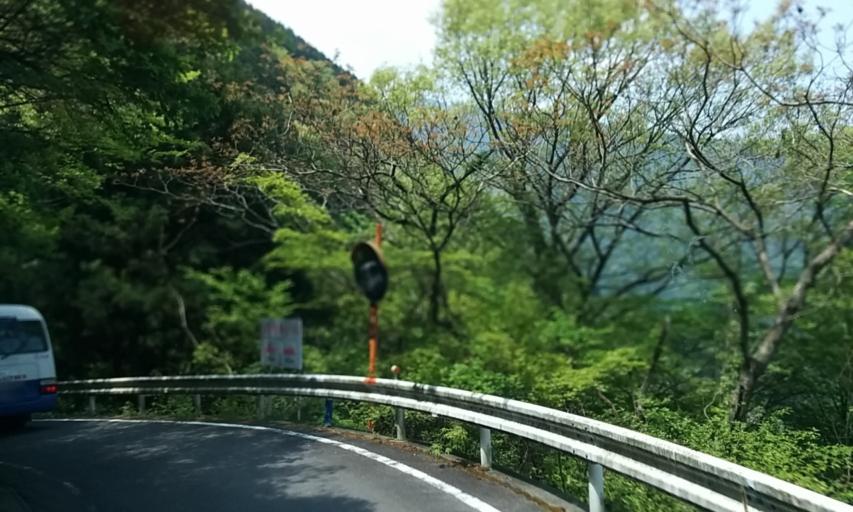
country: JP
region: Ehime
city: Niihama
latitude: 33.8748
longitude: 133.3047
